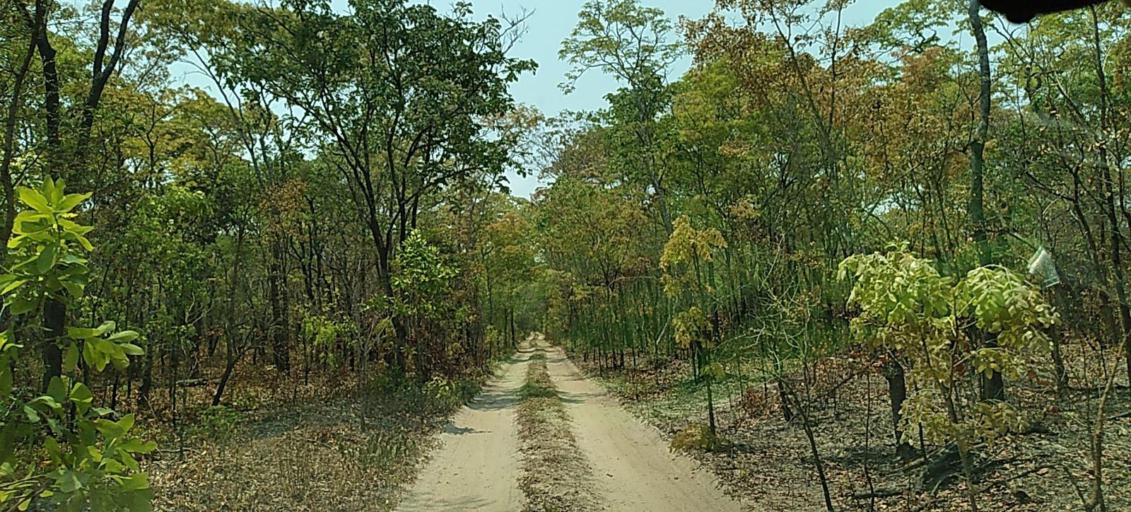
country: ZM
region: North-Western
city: Kabompo
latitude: -13.6492
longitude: 24.4761
